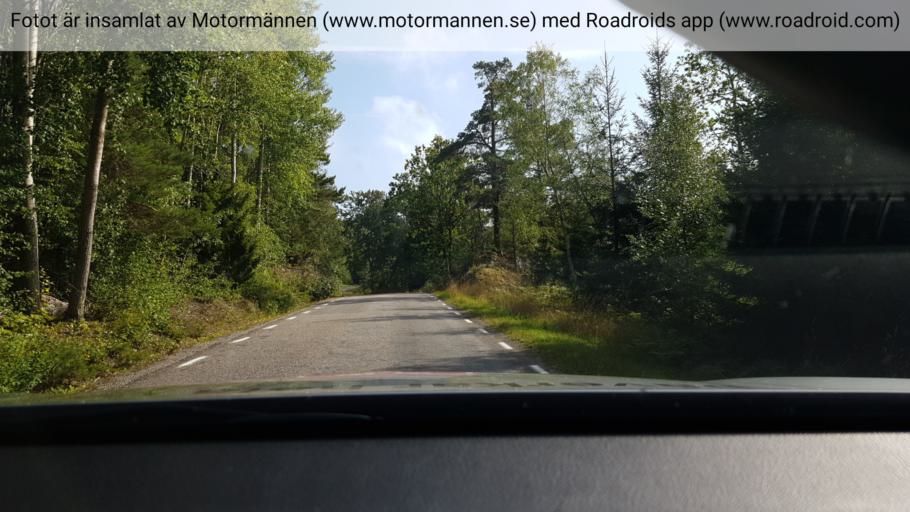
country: SE
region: Stockholm
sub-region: Nynashamns Kommun
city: Osmo
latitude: 58.8820
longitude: 17.7894
